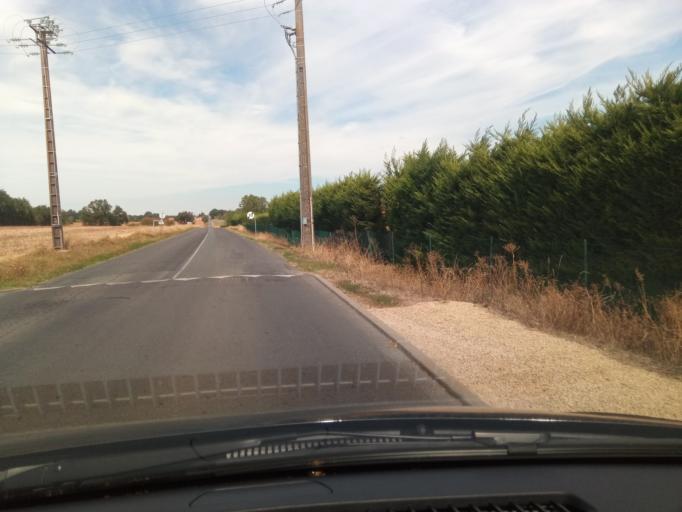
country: FR
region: Poitou-Charentes
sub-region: Departement de la Vienne
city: Terce
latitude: 46.5195
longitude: 0.5668
